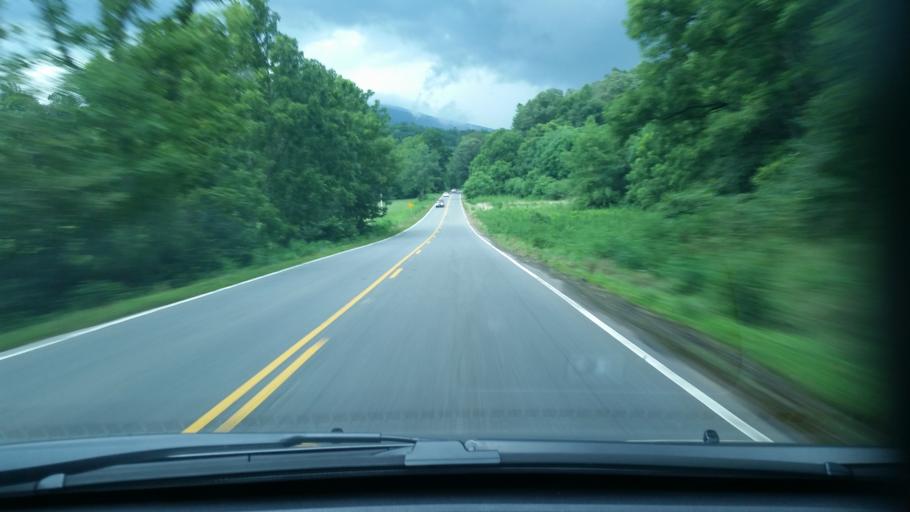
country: US
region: Virginia
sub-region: Nelson County
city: Nellysford
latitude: 37.8919
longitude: -78.8270
